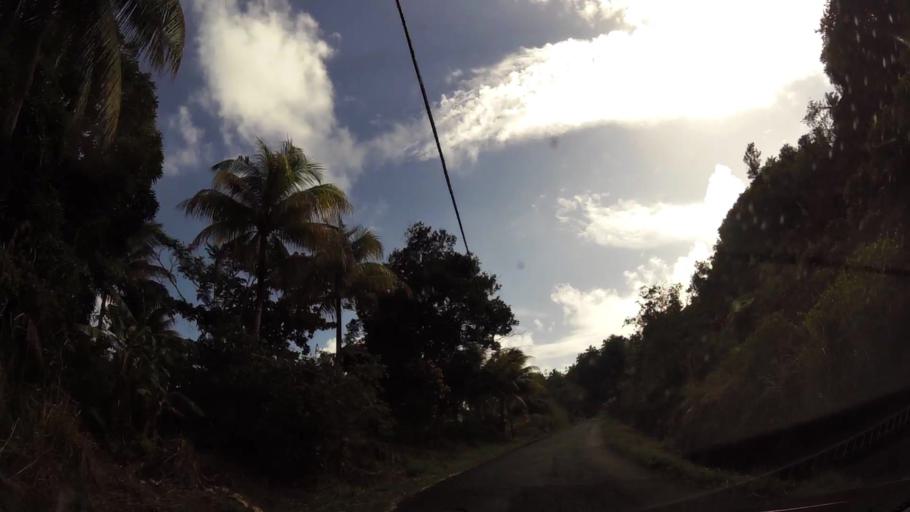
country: DM
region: Saint David
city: Castle Bruce
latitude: 15.4732
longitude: -61.2506
